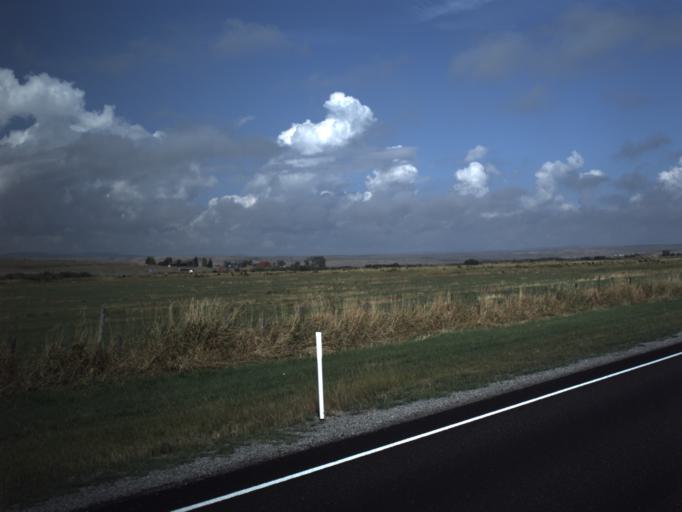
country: US
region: Utah
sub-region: Rich County
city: Randolph
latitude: 41.6190
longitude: -111.1793
